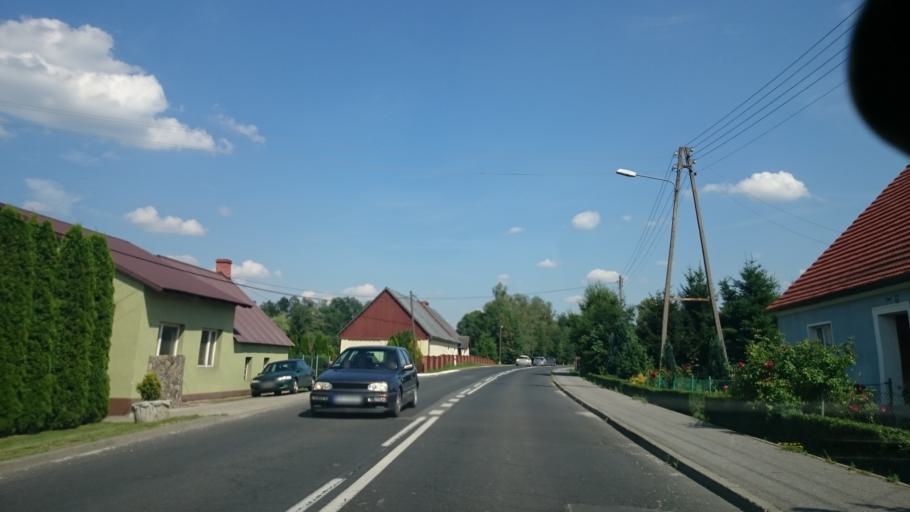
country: PL
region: Lower Silesian Voivodeship
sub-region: Powiat klodzki
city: Ladek-Zdroj
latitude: 50.3462
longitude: 16.7923
